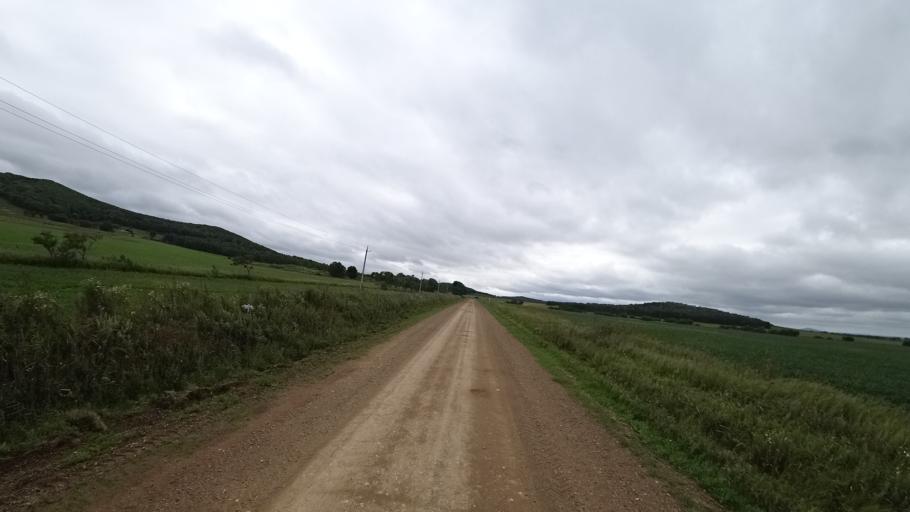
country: RU
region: Primorskiy
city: Chernigovka
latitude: 44.4746
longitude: 132.5802
